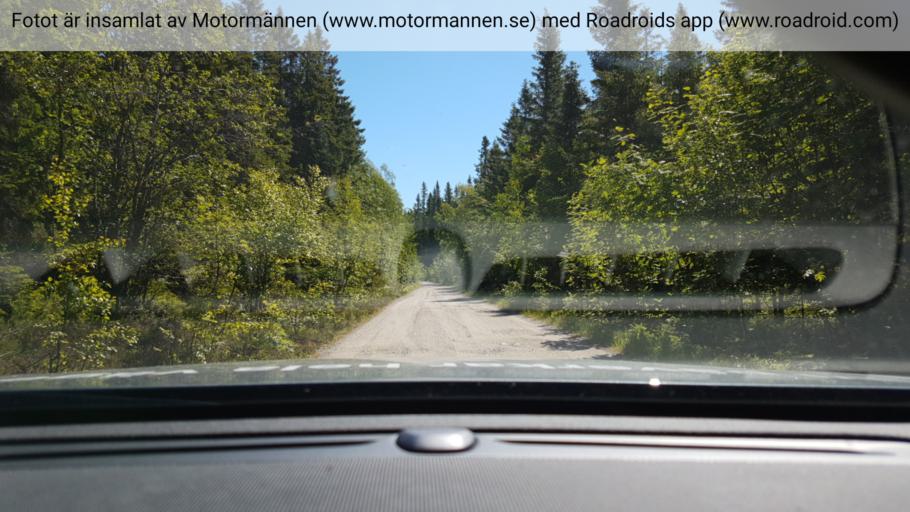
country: SE
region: Vaesterbotten
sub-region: Skelleftea Kommun
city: Skelleftehamn
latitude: 64.4708
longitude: 21.5796
